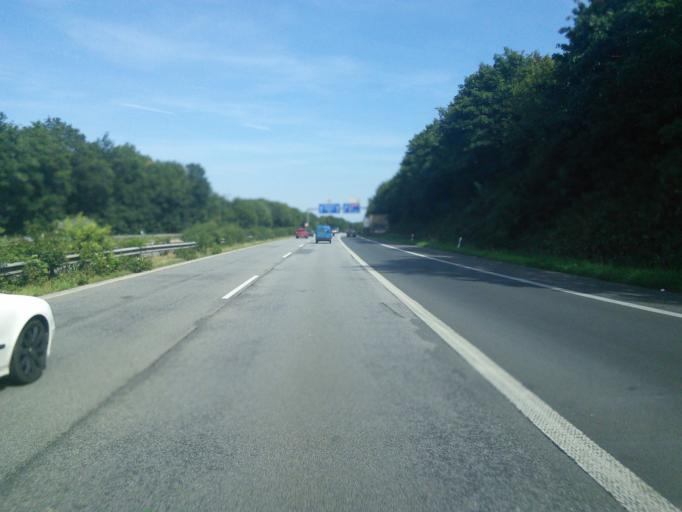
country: DE
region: North Rhine-Westphalia
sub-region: Regierungsbezirk Dusseldorf
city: Kaarst
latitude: 51.2375
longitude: 6.6168
